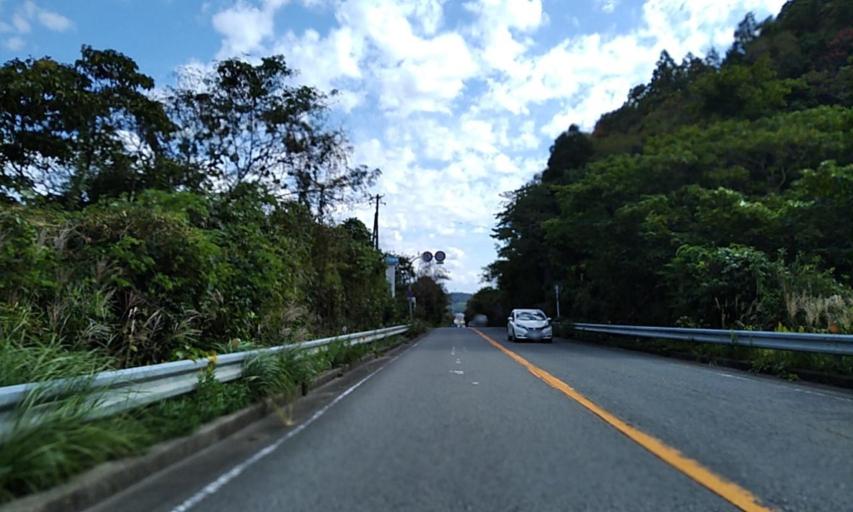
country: JP
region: Wakayama
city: Gobo
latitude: 33.9355
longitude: 135.1363
